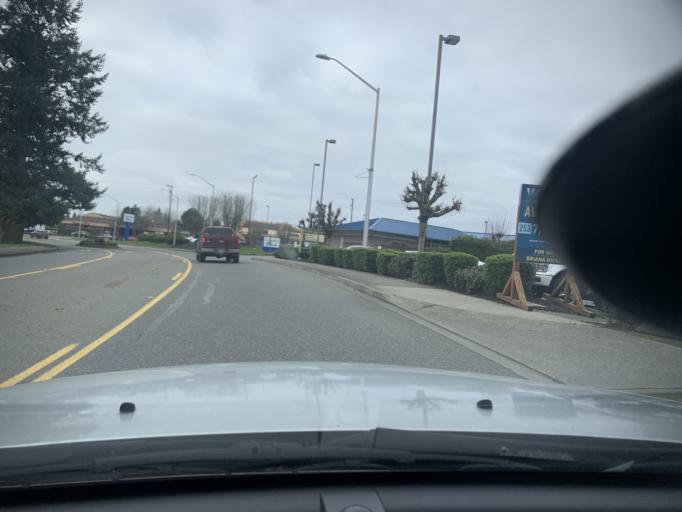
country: US
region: Washington
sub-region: Pierce County
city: Fircrest
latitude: 47.2388
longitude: -122.5245
